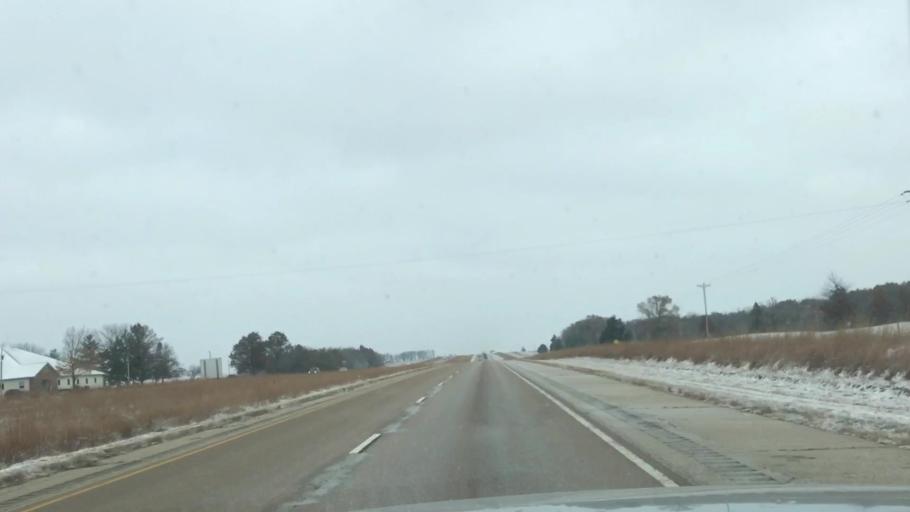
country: US
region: Illinois
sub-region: Montgomery County
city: Raymond
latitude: 39.2906
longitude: -89.6419
